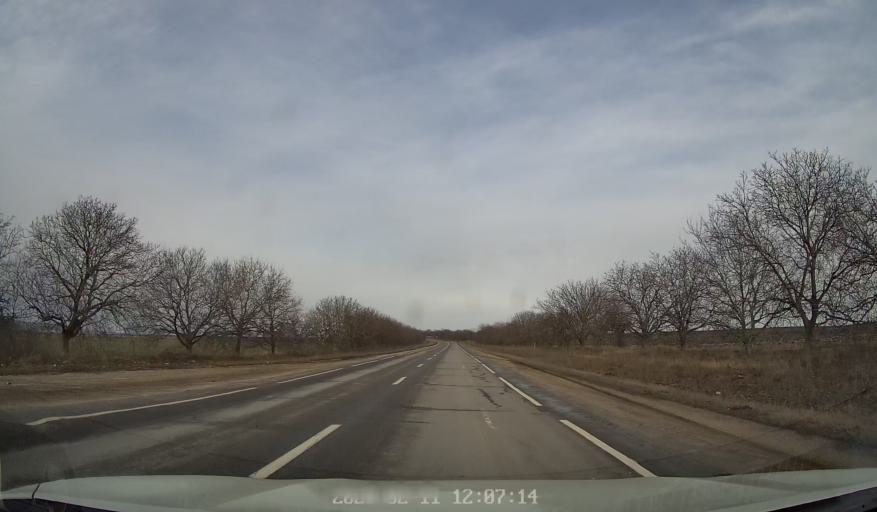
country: MD
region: Riscani
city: Riscani
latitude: 48.0078
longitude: 27.5684
